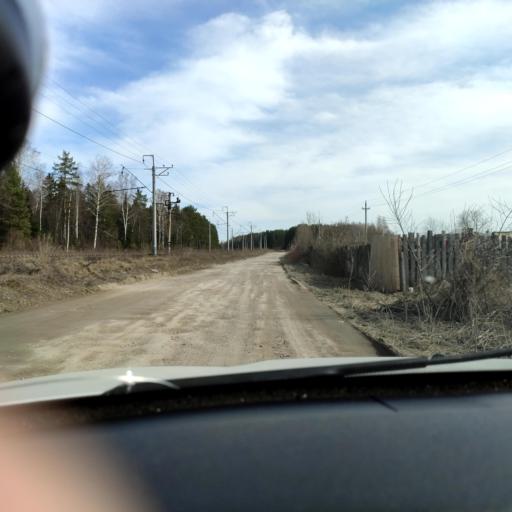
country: RU
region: Perm
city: Overyata
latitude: 58.0590
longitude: 55.9901
